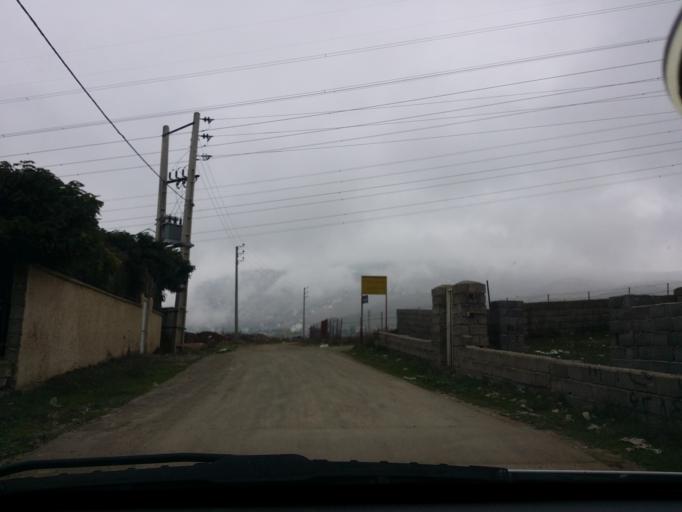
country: IR
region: Mazandaran
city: Chalus
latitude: 36.5129
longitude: 51.2296
